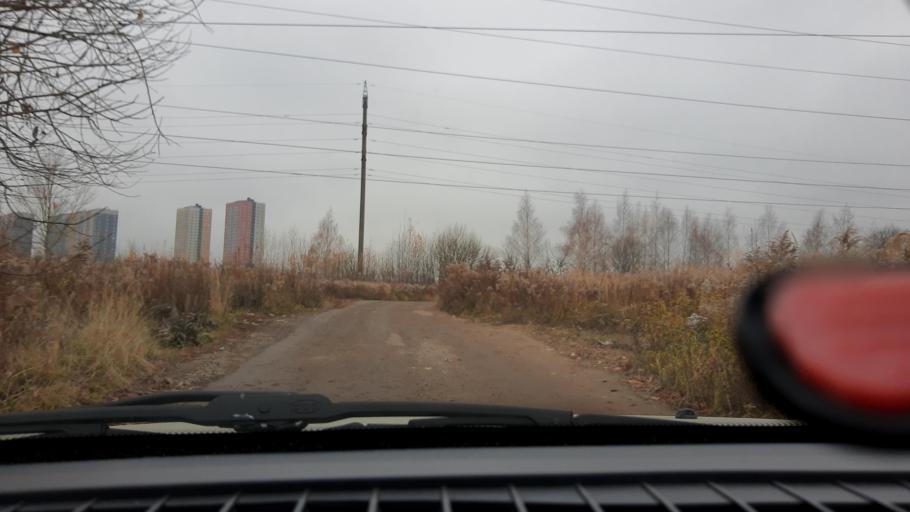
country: RU
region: Nizjnij Novgorod
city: Afonino
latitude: 56.2547
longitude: 44.0502
